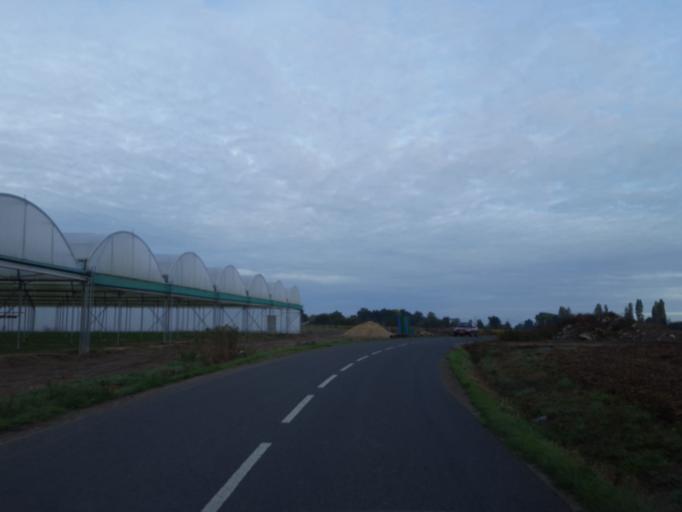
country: FR
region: Pays de la Loire
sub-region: Departement de la Loire-Atlantique
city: Saint-Julien-de-Concelles
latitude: 47.2379
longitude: -1.3896
